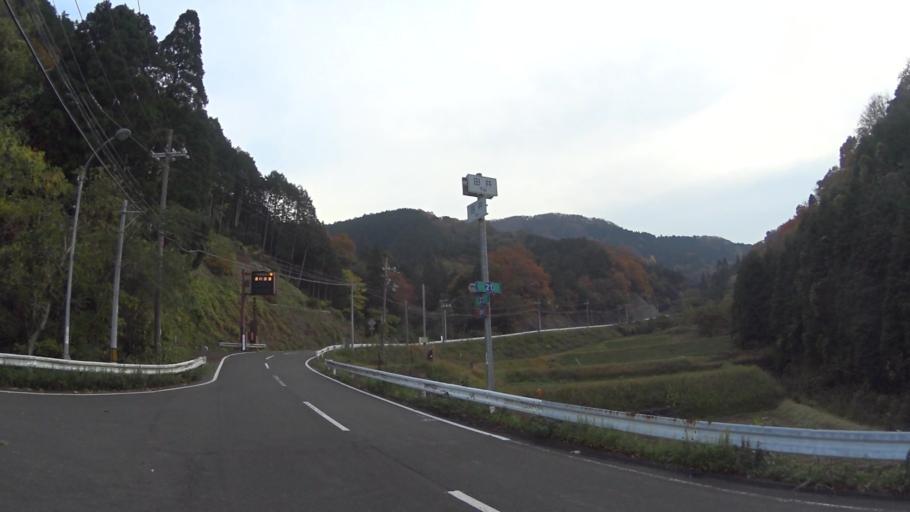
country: JP
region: Kyoto
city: Maizuru
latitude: 35.5600
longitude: 135.4553
